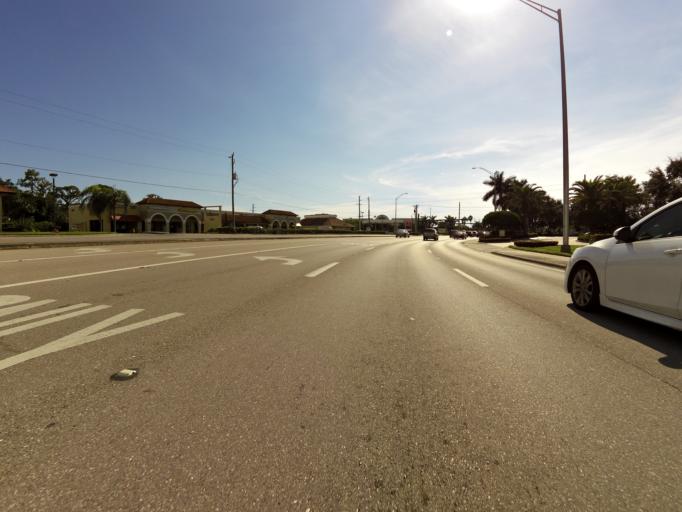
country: US
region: Florida
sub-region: Collier County
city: Naples
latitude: 26.1721
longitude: -81.7899
